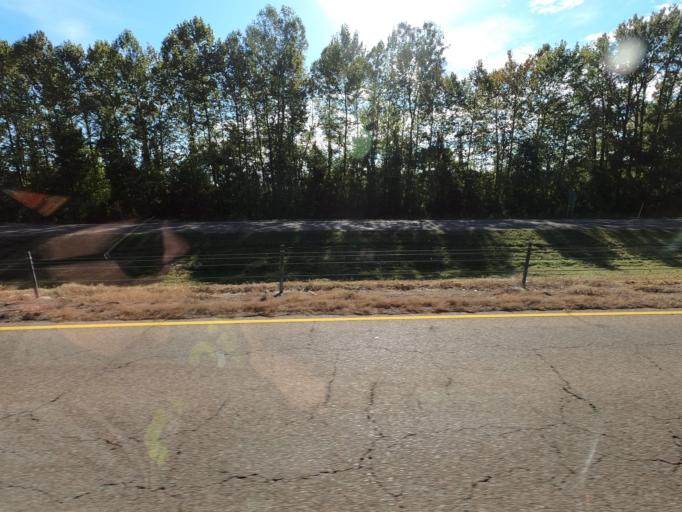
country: US
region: Tennessee
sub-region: Tipton County
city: Brighton
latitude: 35.5024
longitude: -89.7178
